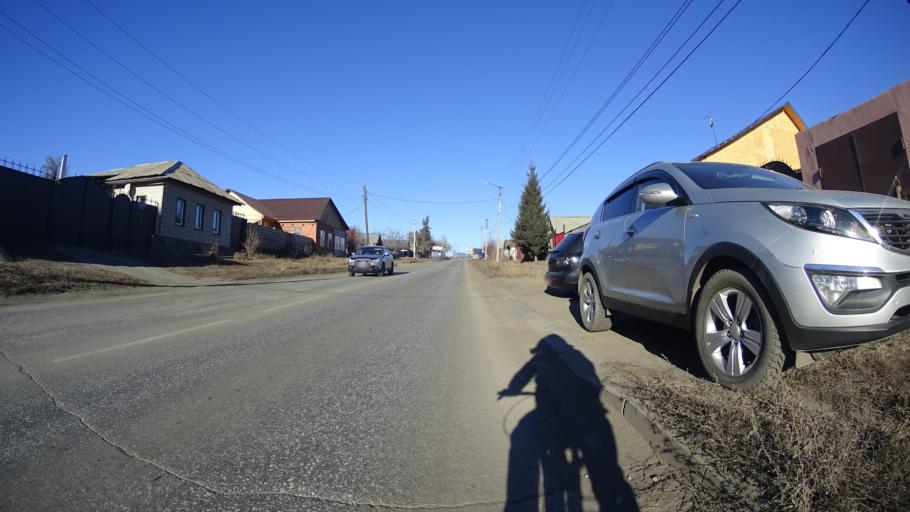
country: RU
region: Chelyabinsk
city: Troitsk
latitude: 54.1018
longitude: 61.5624
